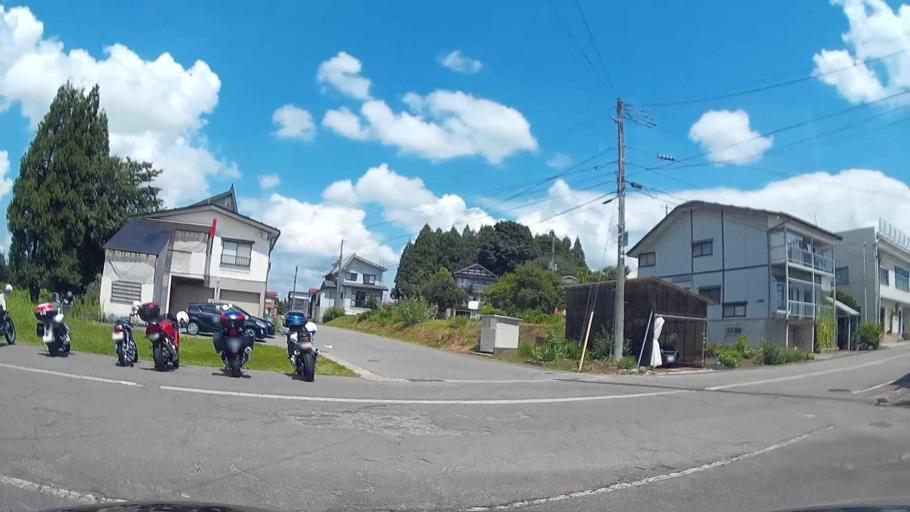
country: JP
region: Niigata
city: Tokamachi
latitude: 37.0972
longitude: 138.7297
